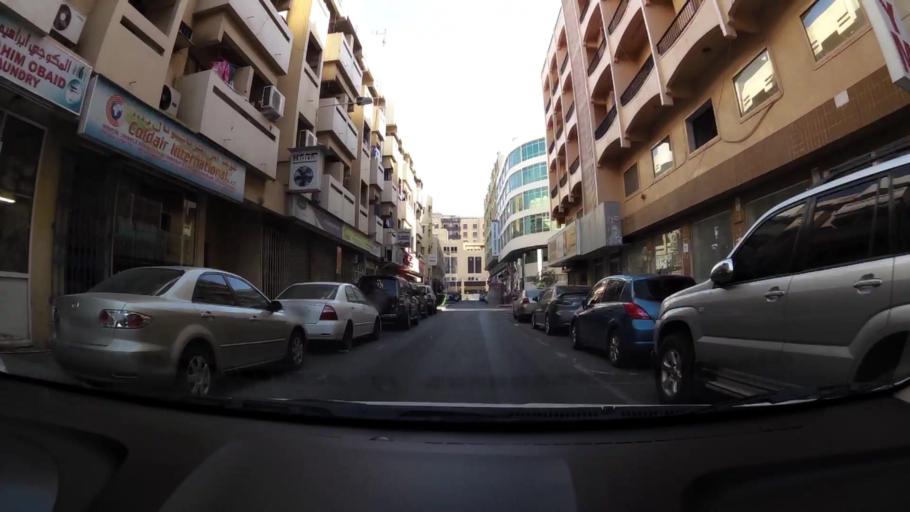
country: AE
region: Ash Shariqah
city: Sharjah
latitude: 25.2687
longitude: 55.3136
